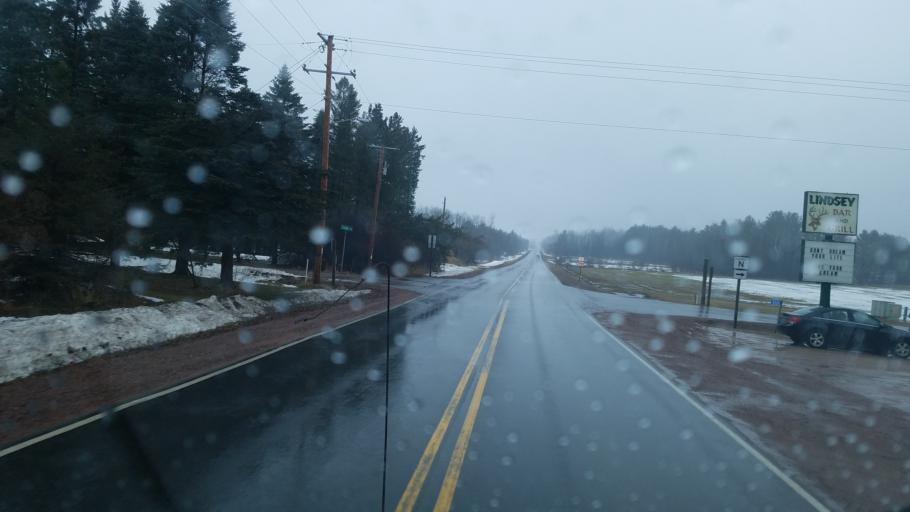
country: US
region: Wisconsin
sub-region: Wood County
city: Marshfield
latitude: 44.5554
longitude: -90.3000
